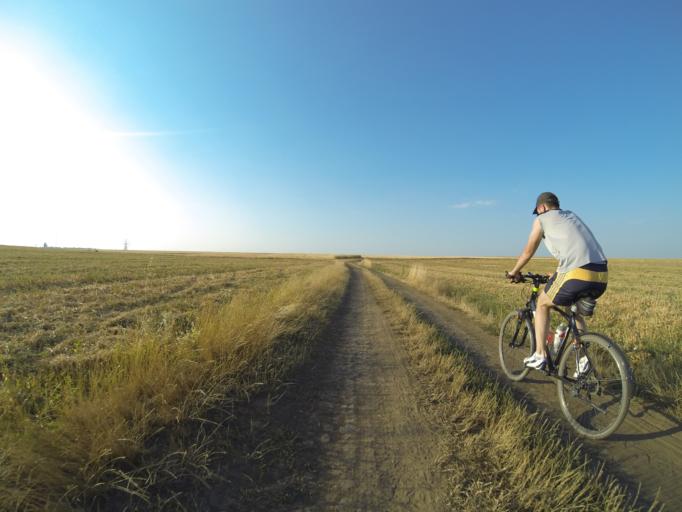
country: RO
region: Dolj
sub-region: Comuna Ceratu
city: Ceratu
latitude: 44.0277
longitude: 23.6729
